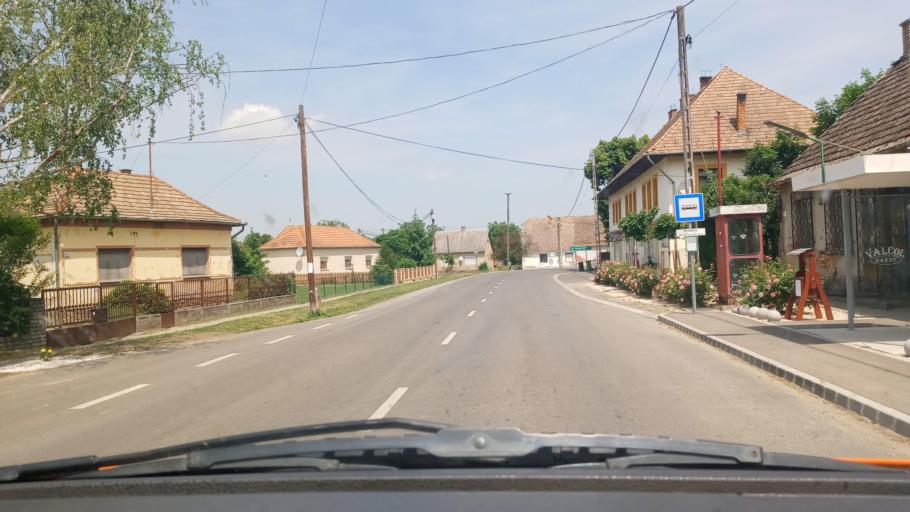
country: HU
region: Baranya
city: Szigetvar
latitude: 45.9742
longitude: 17.7217
